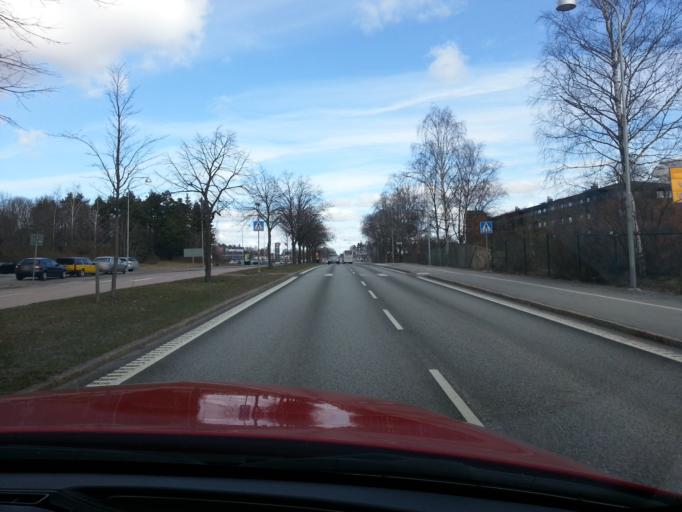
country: SE
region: Uppsala
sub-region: Uppsala Kommun
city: Uppsala
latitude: 59.8732
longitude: 17.6709
